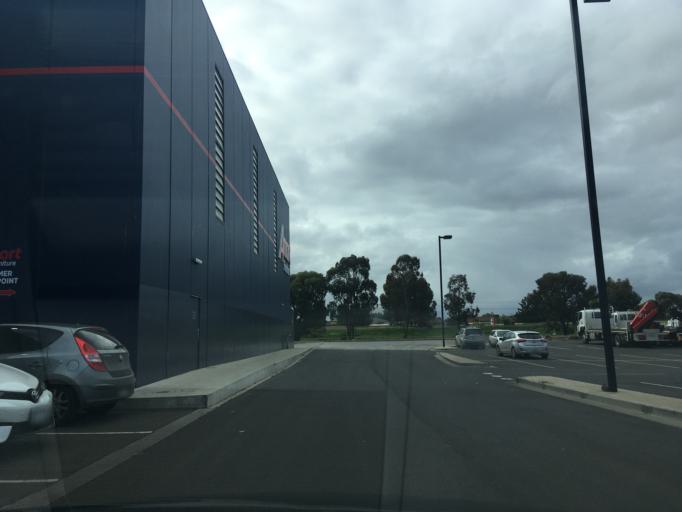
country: AU
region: Victoria
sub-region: Wyndham
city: Hoppers Crossing
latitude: -37.8747
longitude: 144.7120
